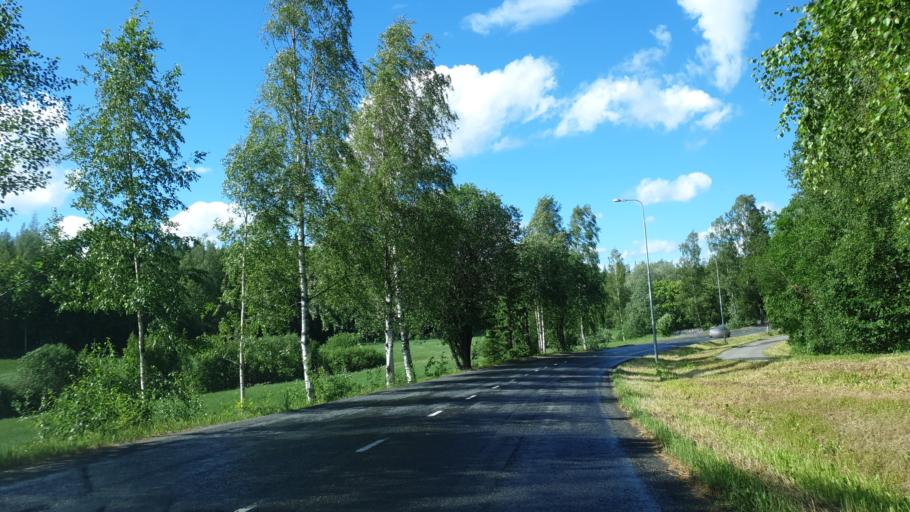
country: FI
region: Northern Savo
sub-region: Kuopio
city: Kuopio
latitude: 62.9184
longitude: 27.6299
